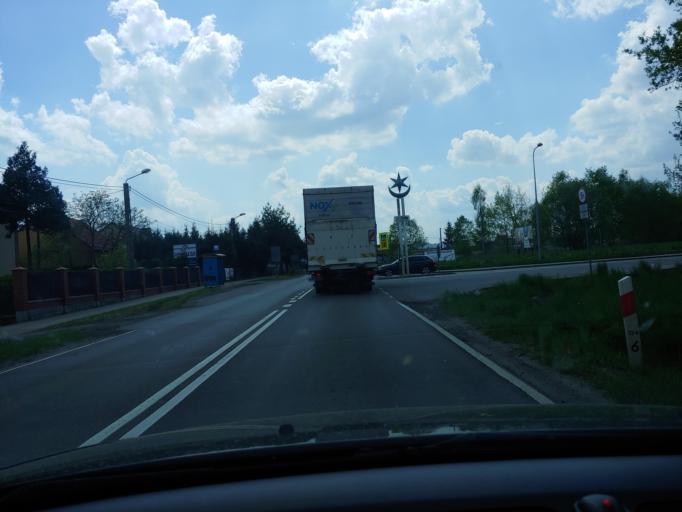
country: PL
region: Lesser Poland Voivodeship
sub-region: Powiat tarnowski
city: Lisia Gora
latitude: 50.0608
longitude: 21.0129
